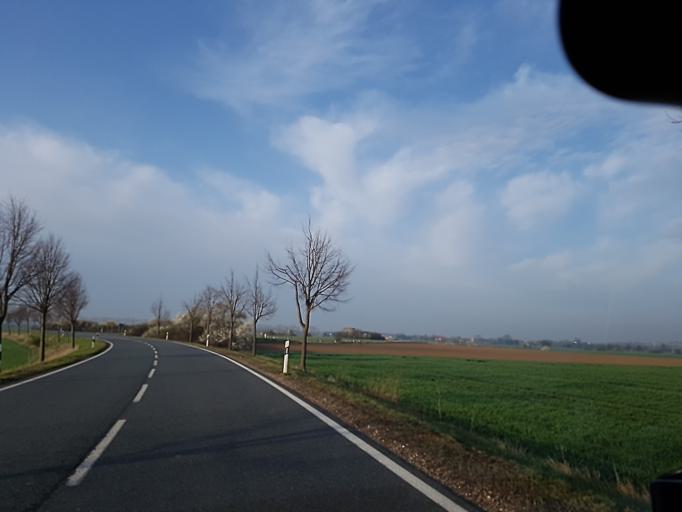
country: DE
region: Saxony
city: Strehla
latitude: 51.3614
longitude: 13.2621
